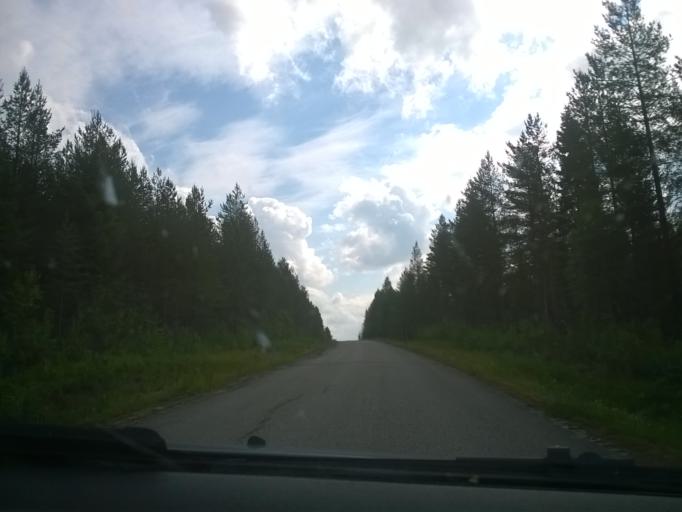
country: FI
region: Kainuu
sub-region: Kehys-Kainuu
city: Kuhmo
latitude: 64.4333
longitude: 29.7160
